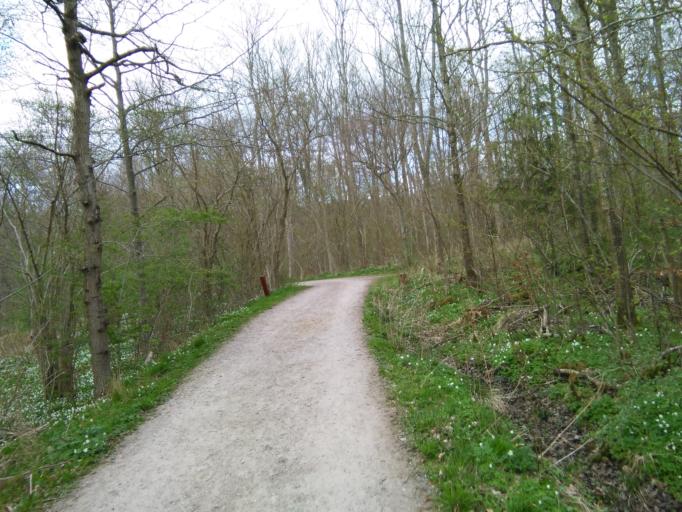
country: DK
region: Central Jutland
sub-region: Arhus Kommune
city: Beder
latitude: 56.0840
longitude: 10.1927
